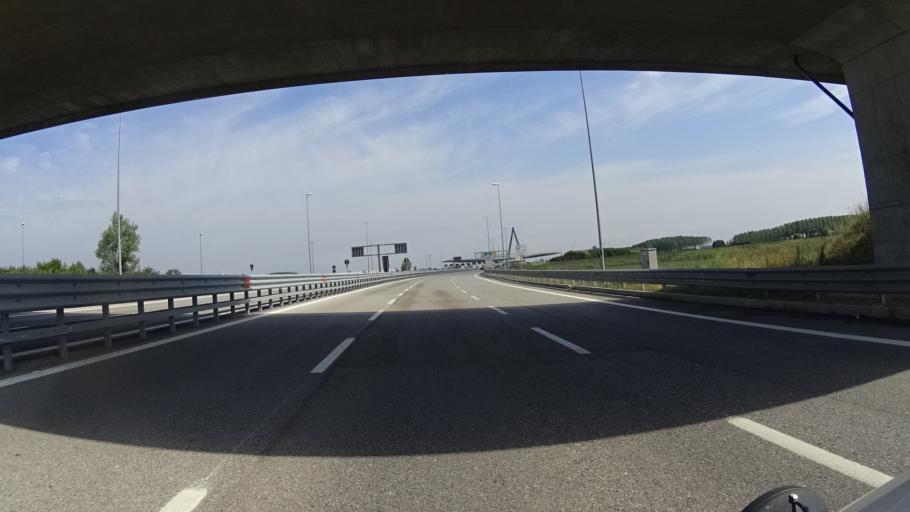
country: IT
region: Friuli Venezia Giulia
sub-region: Provincia di Udine
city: Ronchis
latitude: 45.8011
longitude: 13.0223
